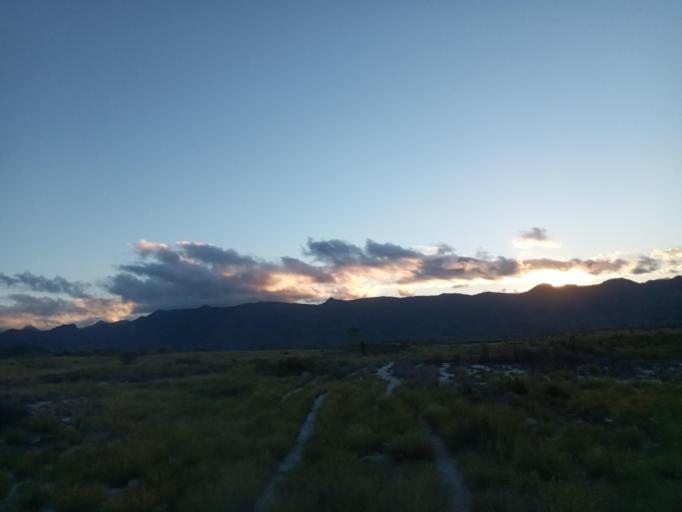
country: MG
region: Anosy
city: Fort Dauphin
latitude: -24.5137
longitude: 47.2317
